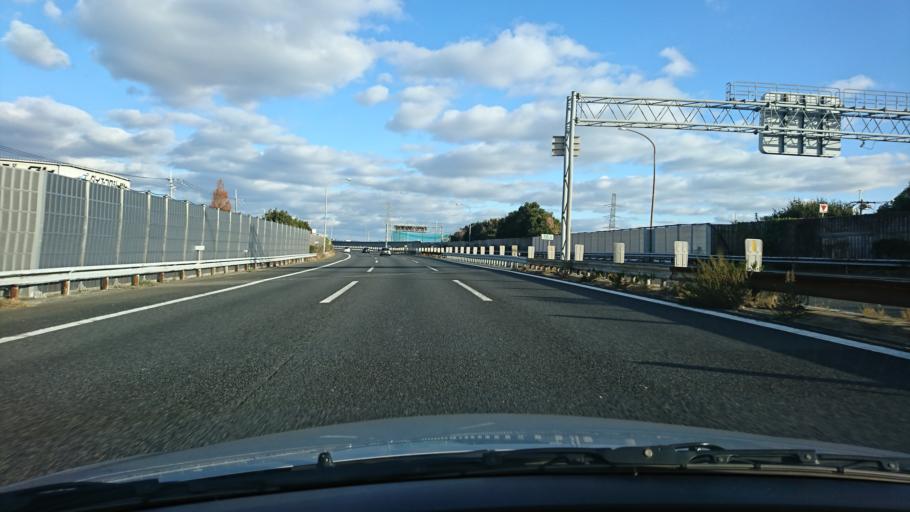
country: JP
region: Hyogo
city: Takarazuka
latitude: 34.8055
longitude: 135.3722
